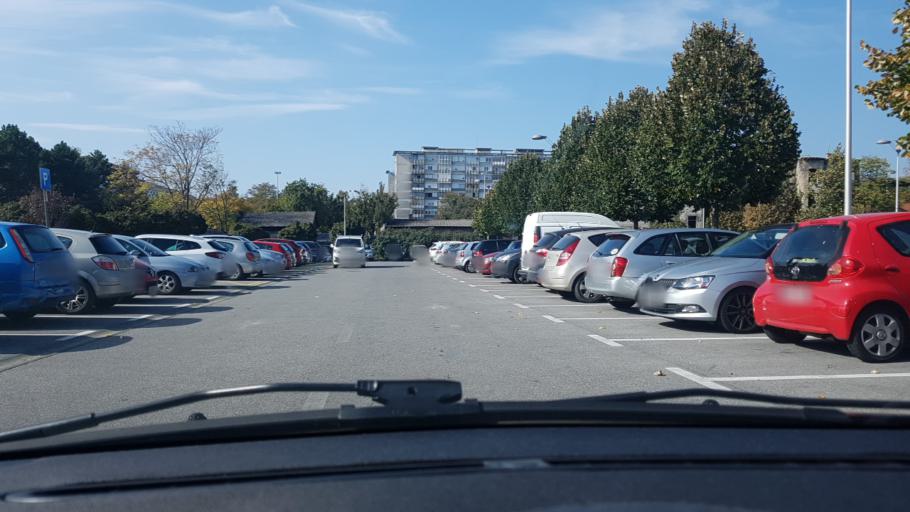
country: HR
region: Grad Zagreb
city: Zagreb - Centar
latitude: 45.8021
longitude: 15.9798
